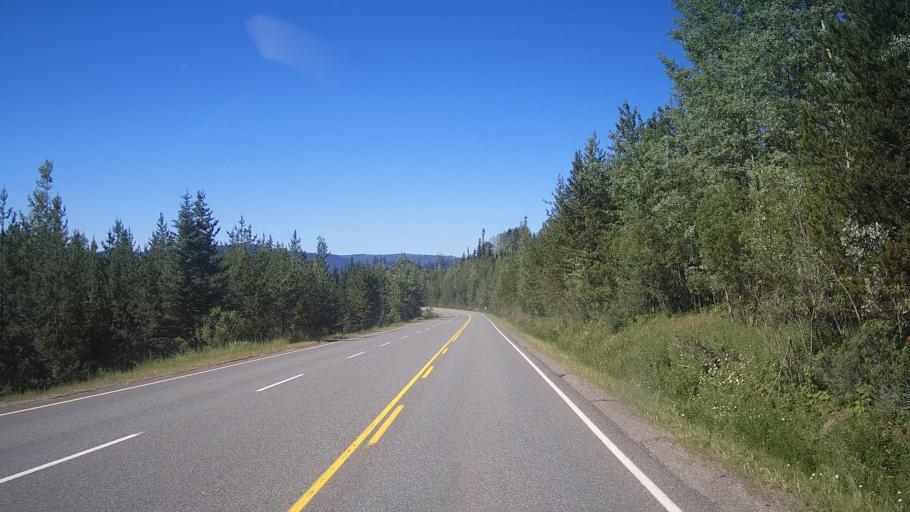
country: CA
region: British Columbia
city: Kamloops
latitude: 51.4914
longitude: -120.4571
